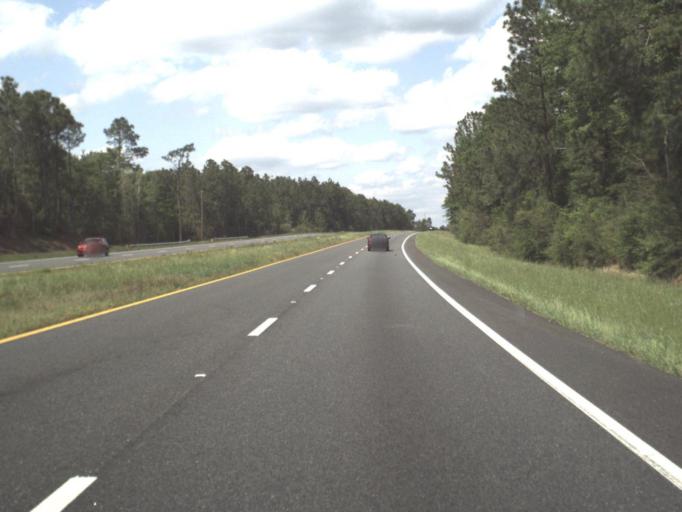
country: US
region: Florida
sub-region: Escambia County
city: Molino
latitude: 30.8264
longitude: -87.3332
